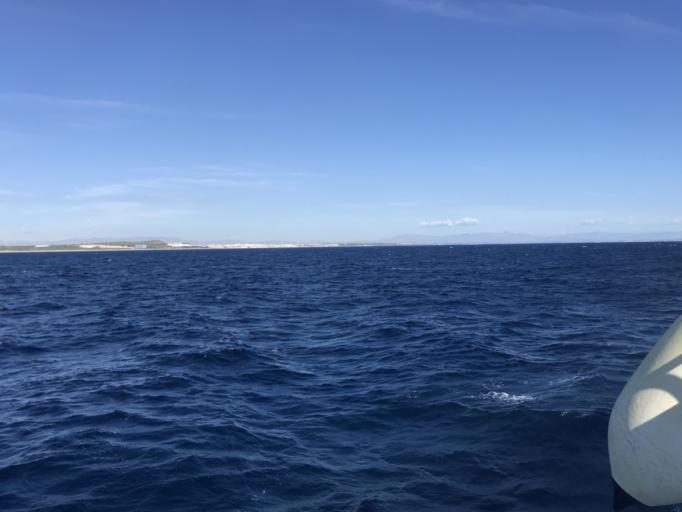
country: ES
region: Valencia
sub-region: Provincia de Alicante
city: Guardamar del Segura
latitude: 38.0291
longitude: -0.6160
